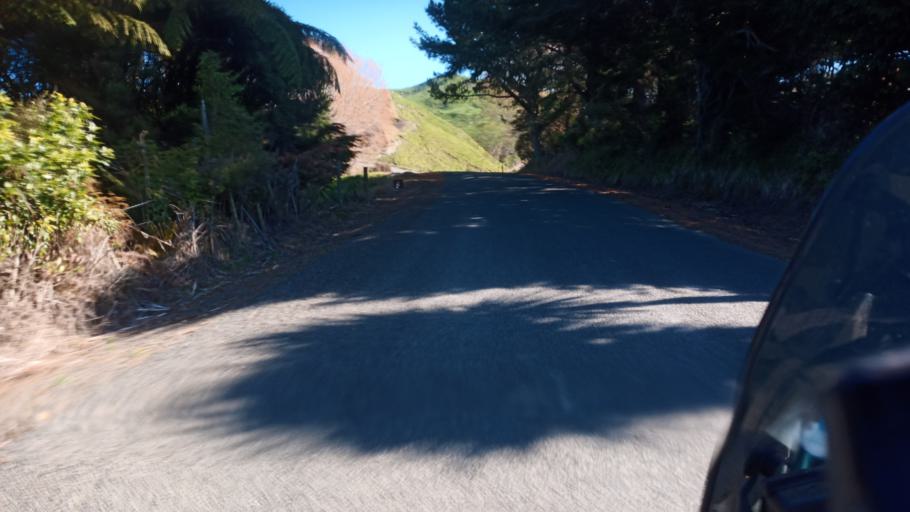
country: NZ
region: Gisborne
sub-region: Gisborne District
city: Gisborne
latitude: -39.1547
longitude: 177.9123
